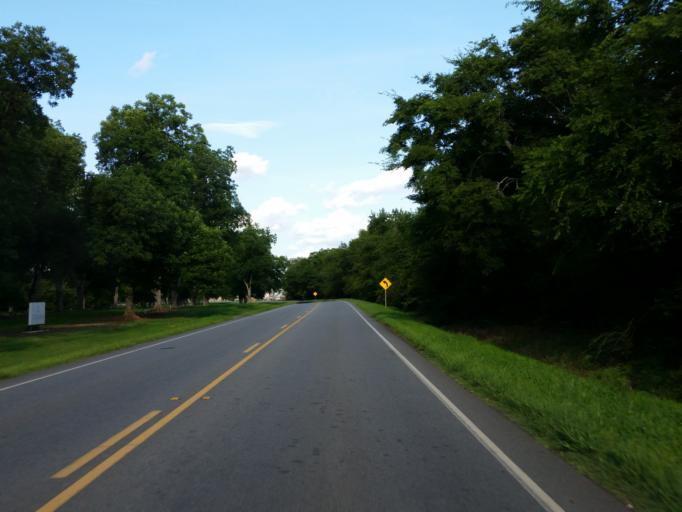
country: US
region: Georgia
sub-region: Crisp County
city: Cordele
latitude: 31.9579
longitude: -83.9820
